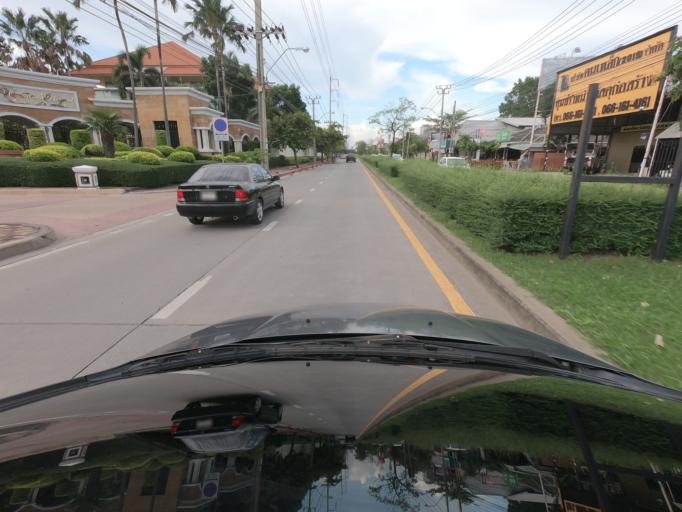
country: TH
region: Bangkok
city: Bang Na
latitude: 13.6560
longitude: 100.6221
